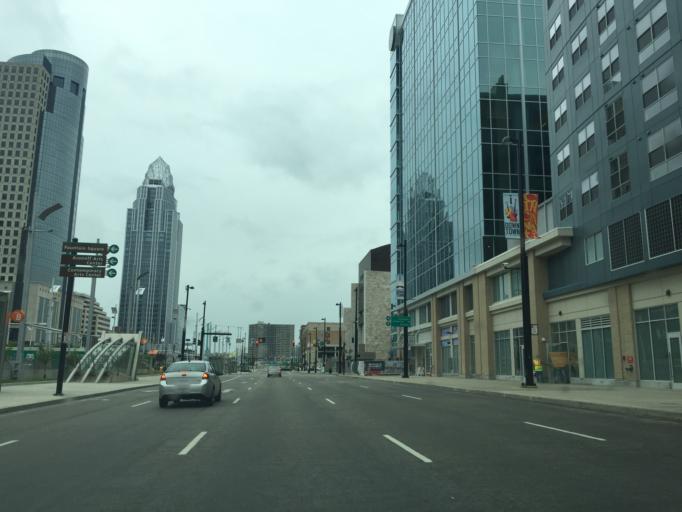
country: US
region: Kentucky
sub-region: Kenton County
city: Covington
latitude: 39.0978
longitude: -84.5134
